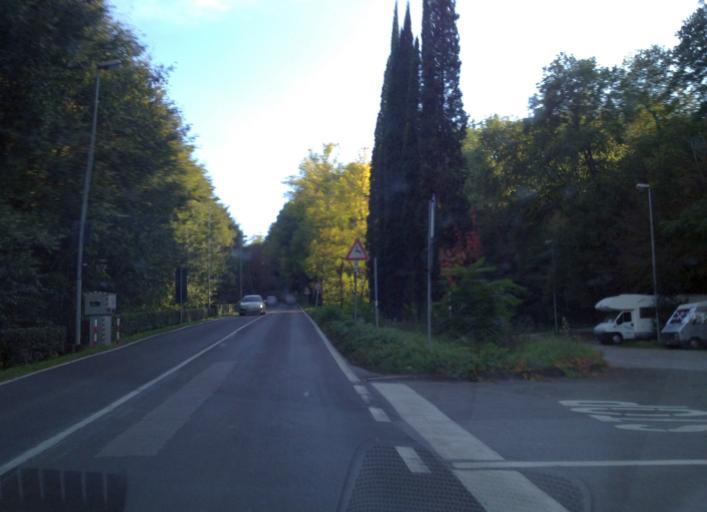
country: IT
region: Tuscany
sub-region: Provincia di Siena
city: Poggibonsi
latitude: 43.4625
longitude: 11.1460
